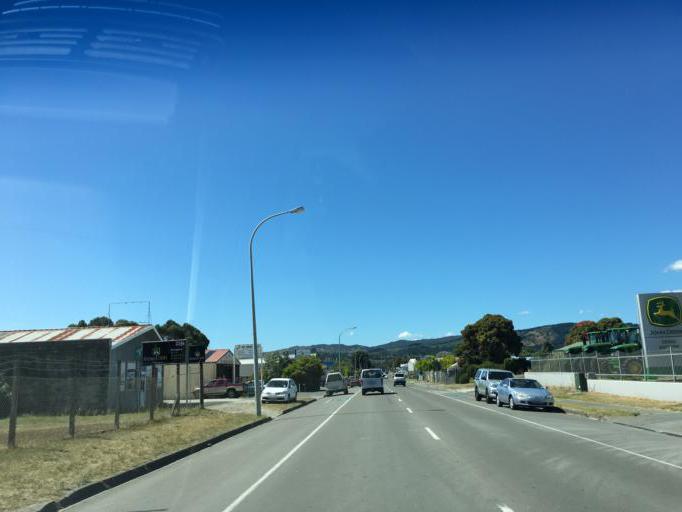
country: NZ
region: Gisborne
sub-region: Gisborne District
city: Gisborne
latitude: -38.6670
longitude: 178.0048
